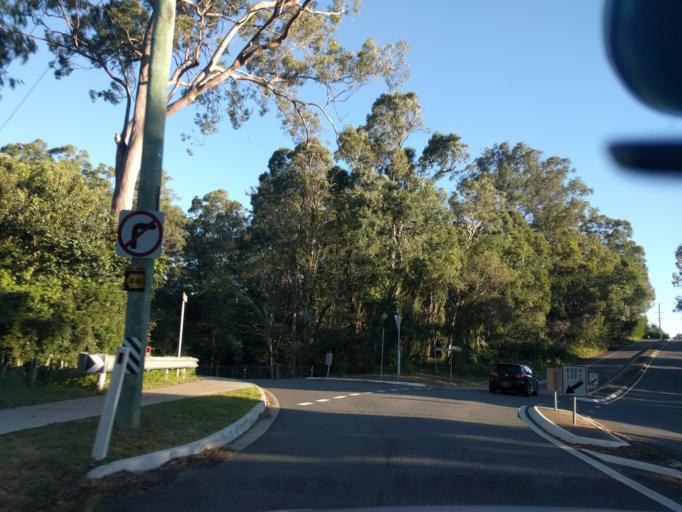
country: AU
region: Queensland
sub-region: Brisbane
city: Seventeen Mile Rocks
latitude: -27.5244
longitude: 152.9562
